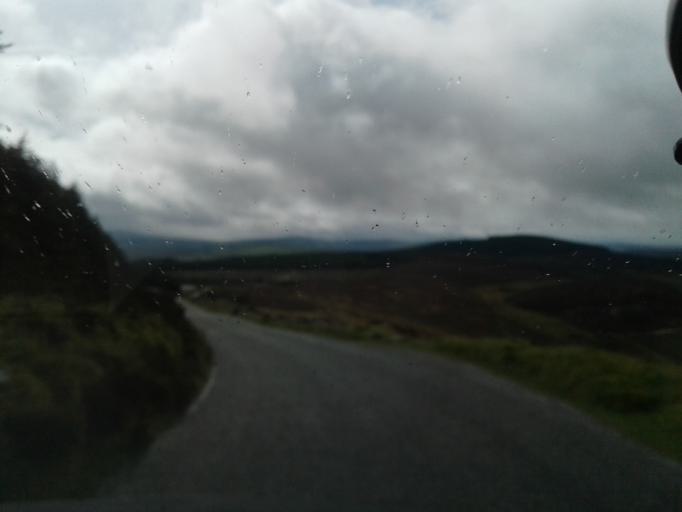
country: IE
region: Leinster
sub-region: Wicklow
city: Enniskerry
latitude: 53.1020
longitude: -6.2543
